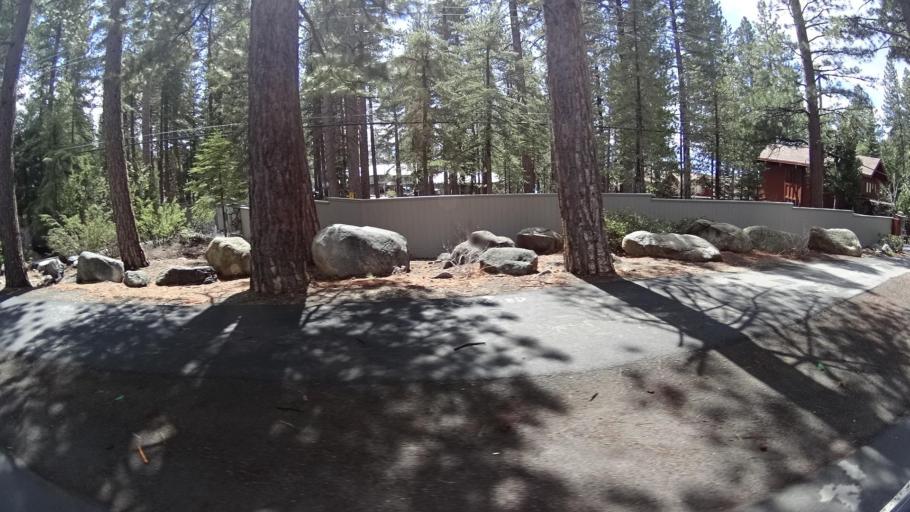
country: US
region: Nevada
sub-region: Washoe County
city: Incline Village
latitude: 39.2497
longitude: -119.9808
